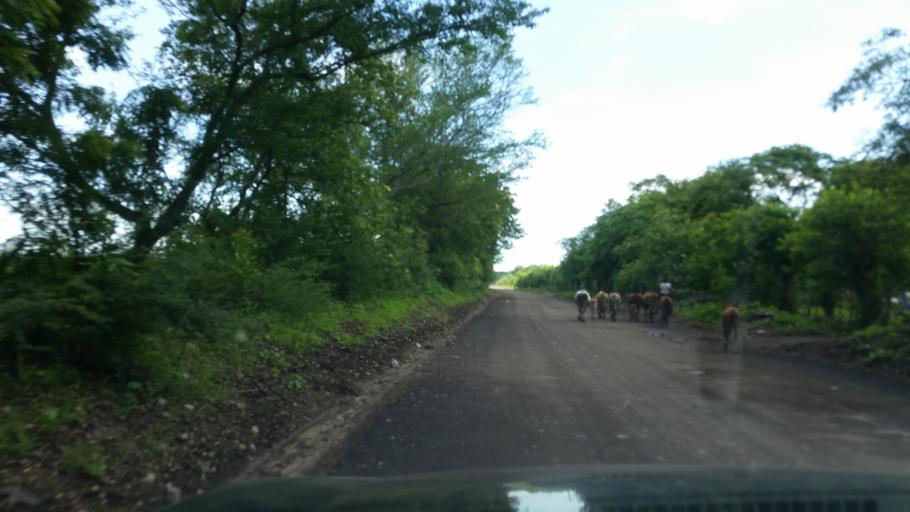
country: NI
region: Chinandega
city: El Viejo
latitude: 12.7463
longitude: -87.1341
